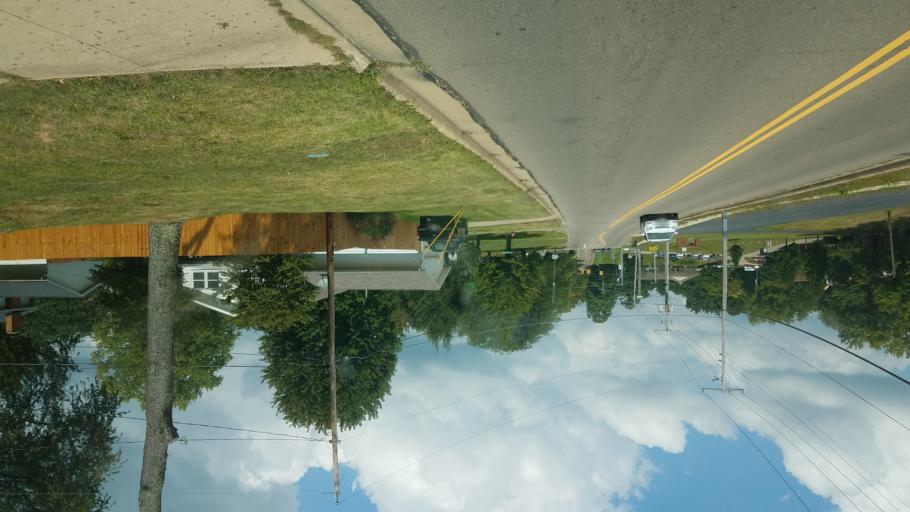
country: US
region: Ohio
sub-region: Knox County
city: Mount Vernon
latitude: 40.3864
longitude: -82.4636
